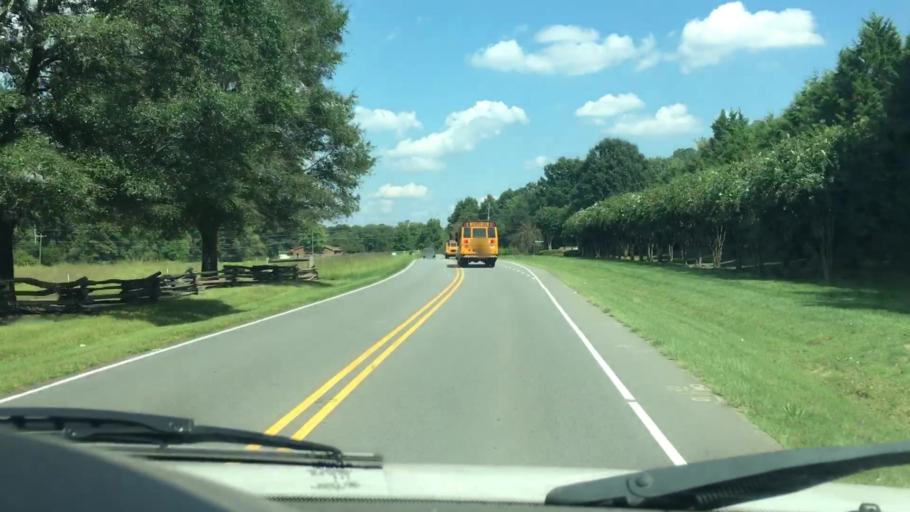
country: US
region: North Carolina
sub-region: Mecklenburg County
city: Huntersville
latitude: 35.3603
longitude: -80.8655
